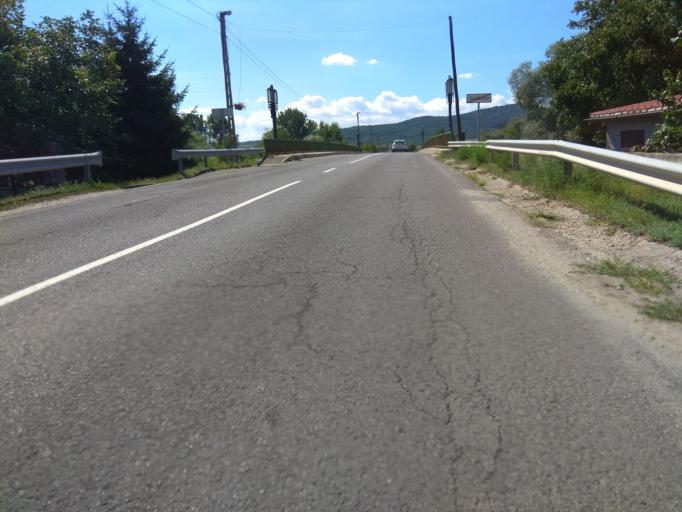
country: HU
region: Borsod-Abauj-Zemplen
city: Sajokaza
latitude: 48.2820
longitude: 20.5824
